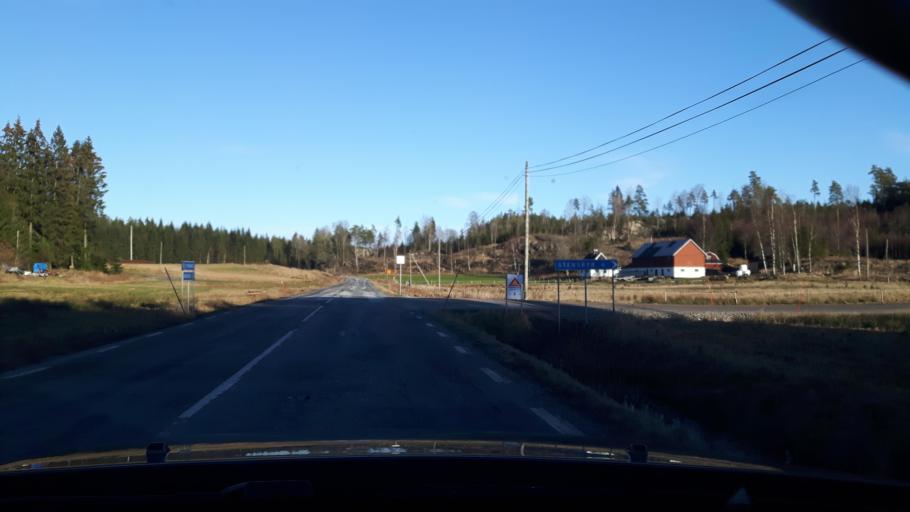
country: SE
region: Vaestra Goetaland
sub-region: Munkedals Kommun
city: Munkedal
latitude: 58.5516
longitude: 11.7193
